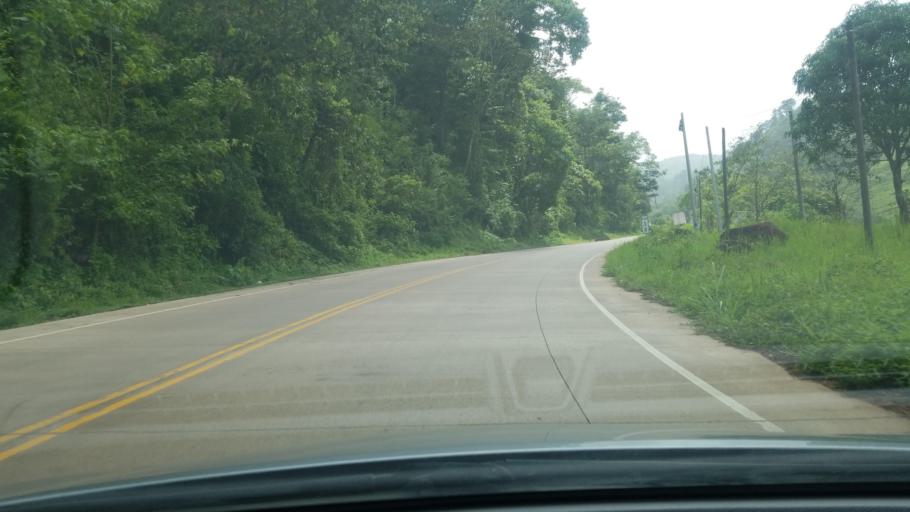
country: HN
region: Copan
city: Buenos Aires
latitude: 14.9217
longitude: -88.9770
